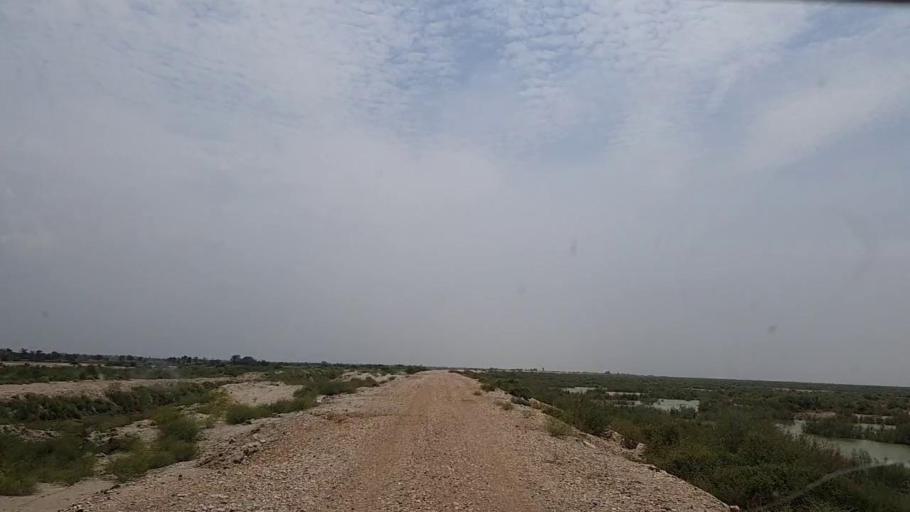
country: PK
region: Sindh
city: Phulji
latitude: 26.8724
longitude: 67.6493
